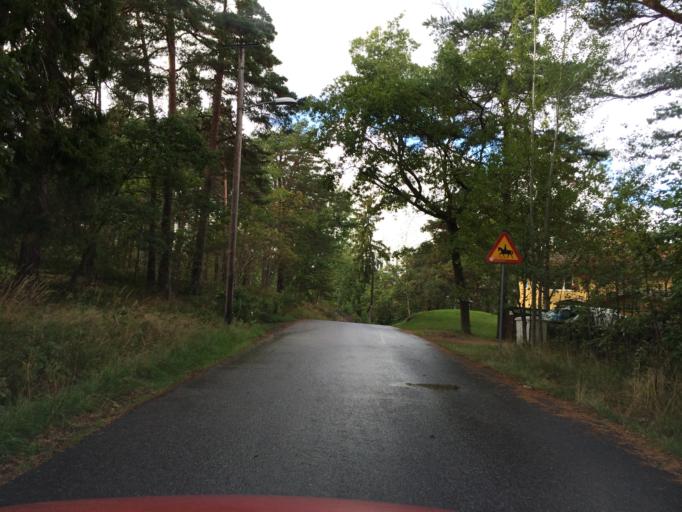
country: SE
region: Stockholm
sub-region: Stockholms Kommun
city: Bromma
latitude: 59.3066
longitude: 17.9698
